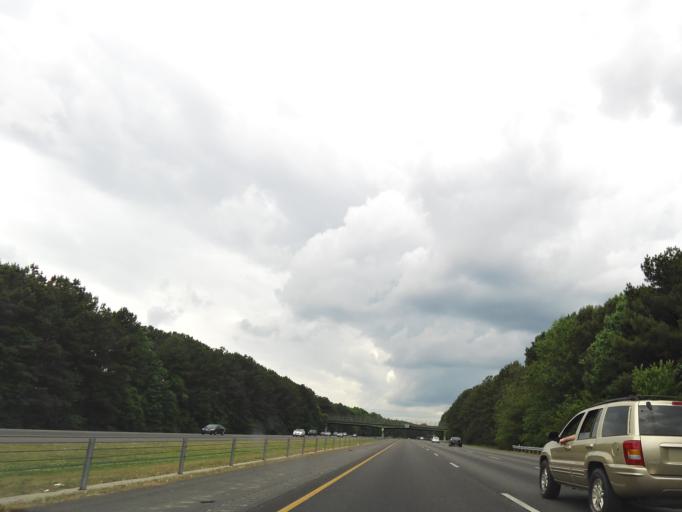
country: US
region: Georgia
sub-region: Douglas County
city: Douglasville
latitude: 33.7245
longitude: -84.7741
